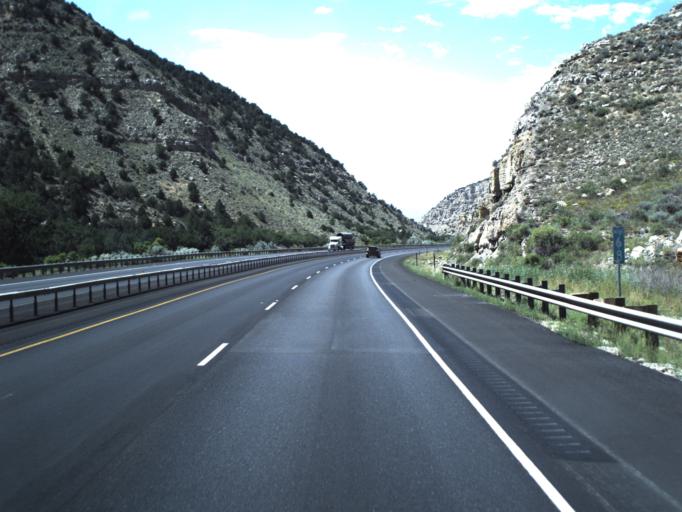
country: US
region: Utah
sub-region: Sevier County
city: Salina
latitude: 38.8983
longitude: -111.6562
